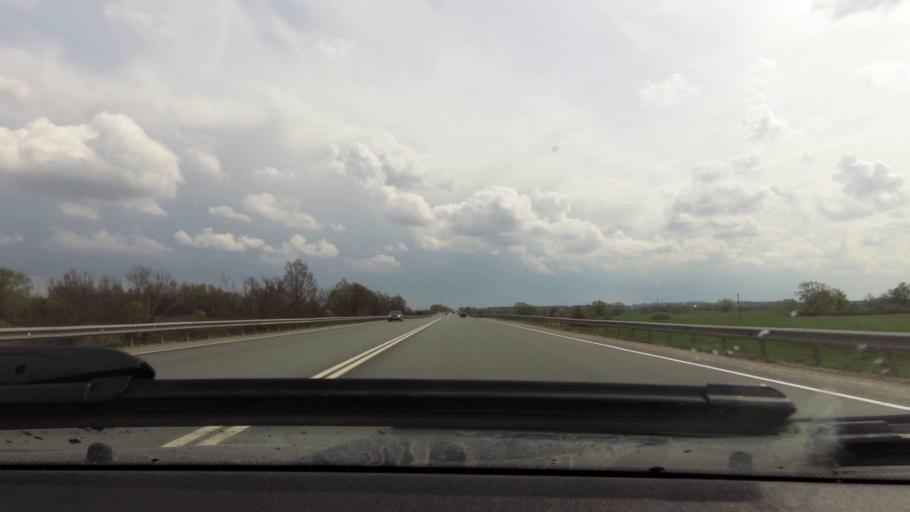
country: RU
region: Rjazan
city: Bagramovo
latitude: 54.7464
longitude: 39.4326
